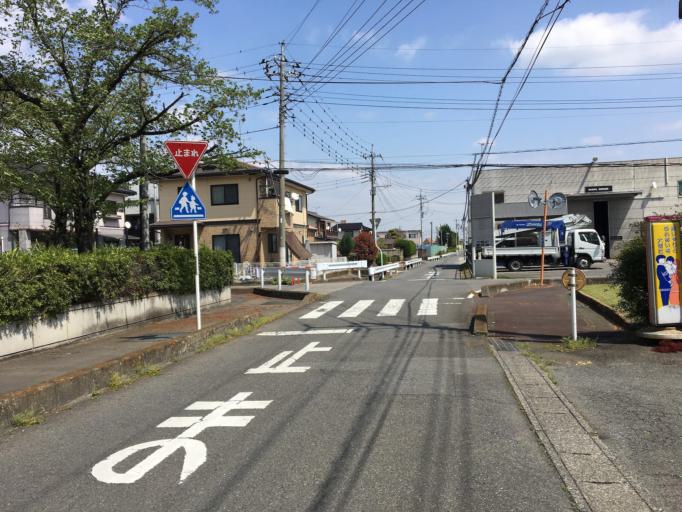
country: JP
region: Gunma
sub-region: Sawa-gun
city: Tamamura
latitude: 36.2887
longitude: 139.1516
